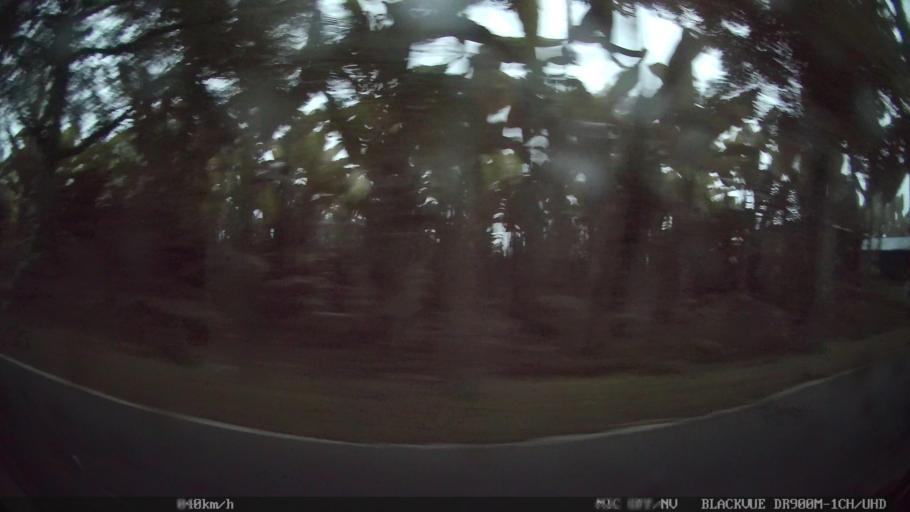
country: ID
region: Bali
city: Banjar Taro Kelod
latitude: -8.3414
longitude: 115.2811
